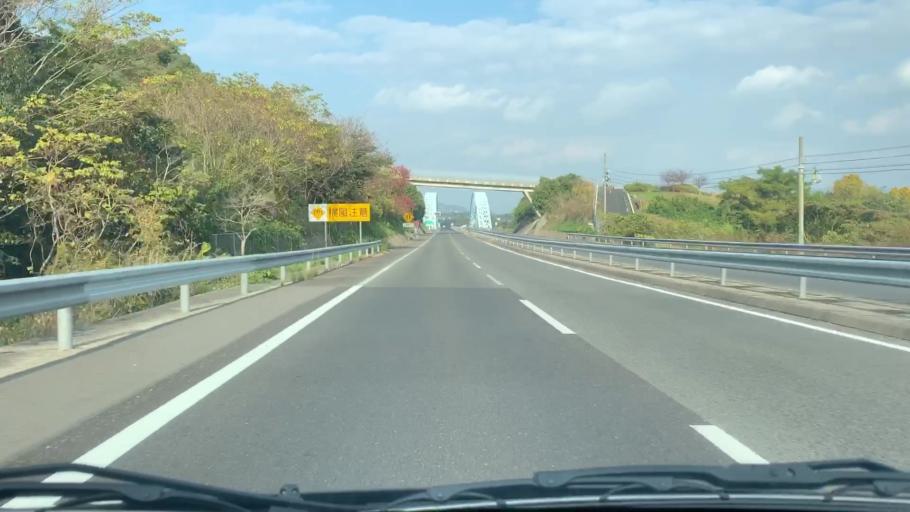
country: JP
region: Nagasaki
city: Sasebo
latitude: 33.0507
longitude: 129.7526
